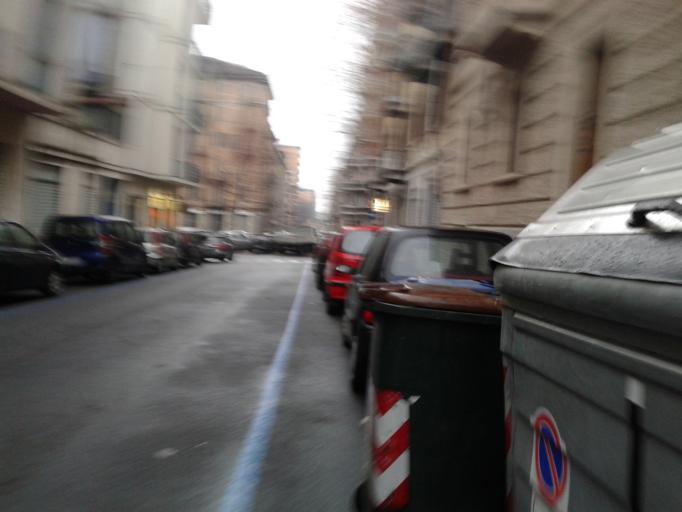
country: IT
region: Piedmont
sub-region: Provincia di Torino
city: Turin
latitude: 45.0815
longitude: 7.6673
